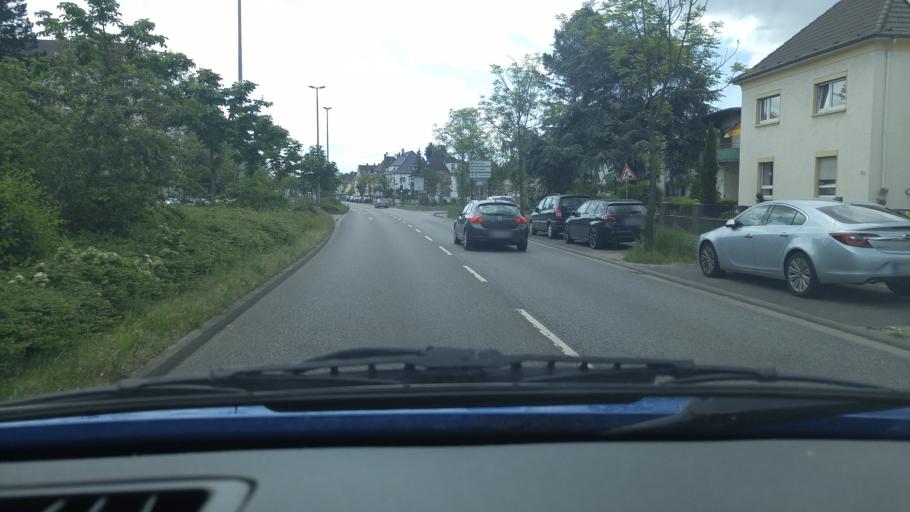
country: DE
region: Hesse
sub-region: Regierungsbezirk Darmstadt
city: Russelsheim
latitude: 50.0004
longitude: 8.4251
